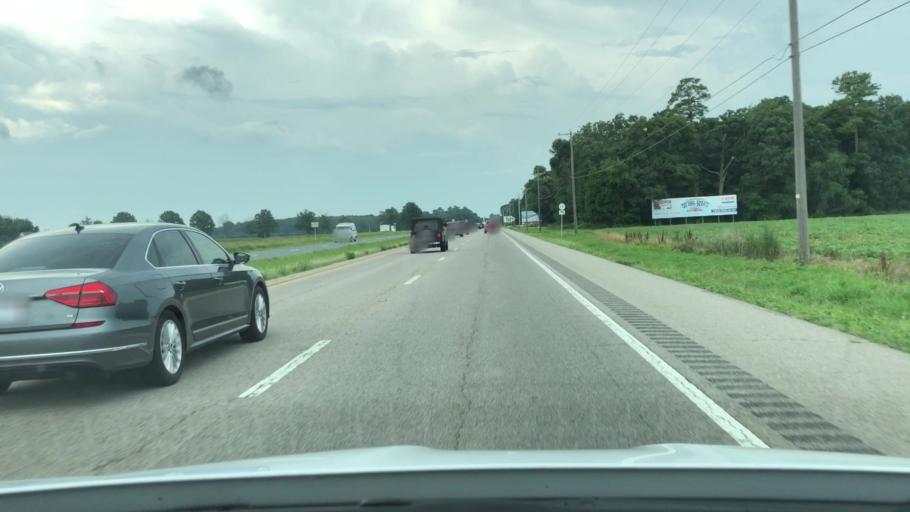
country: US
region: Virginia
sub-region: Northampton County
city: Cape Charles
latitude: 37.2441
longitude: -75.9719
